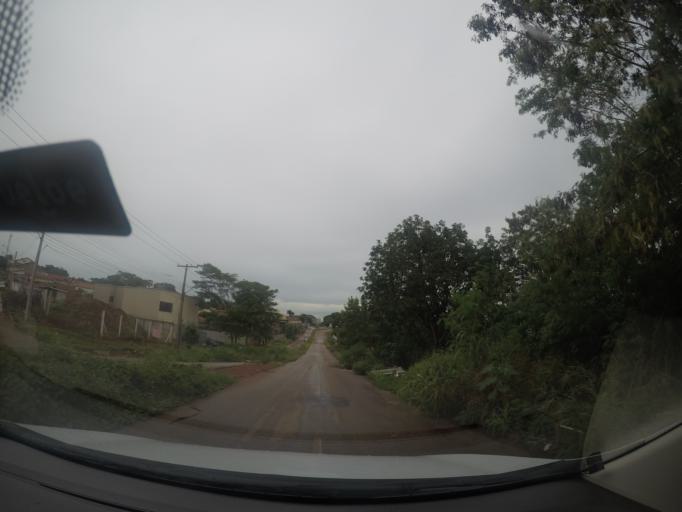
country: BR
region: Goias
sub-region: Goiania
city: Goiania
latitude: -16.6273
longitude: -49.2363
